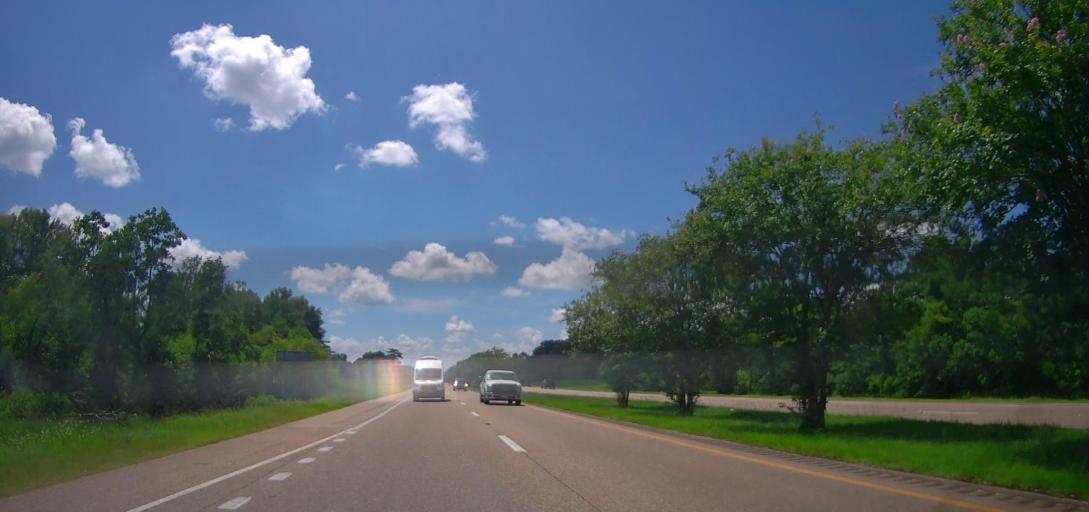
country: US
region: Alabama
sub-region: Montgomery County
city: Montgomery
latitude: 32.4224
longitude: -86.2606
